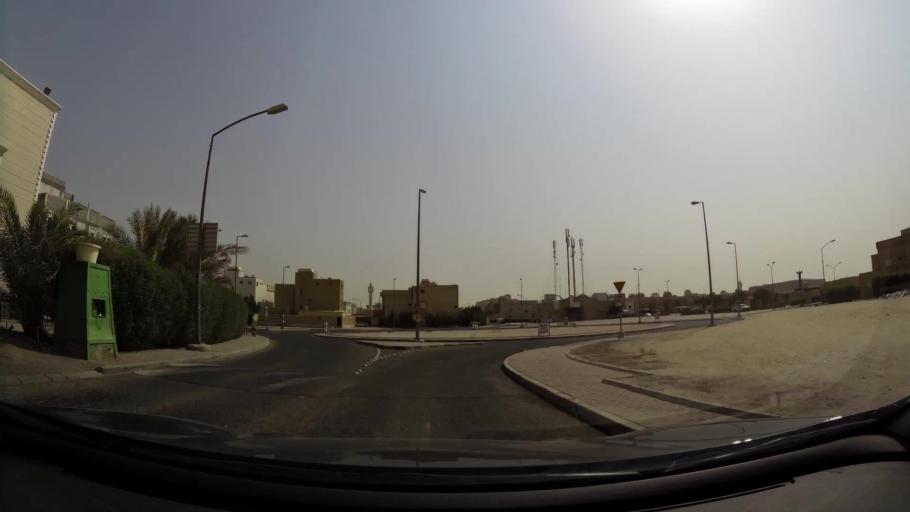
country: KW
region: Muhafazat al Jahra'
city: Al Jahra'
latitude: 29.3237
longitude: 47.7231
